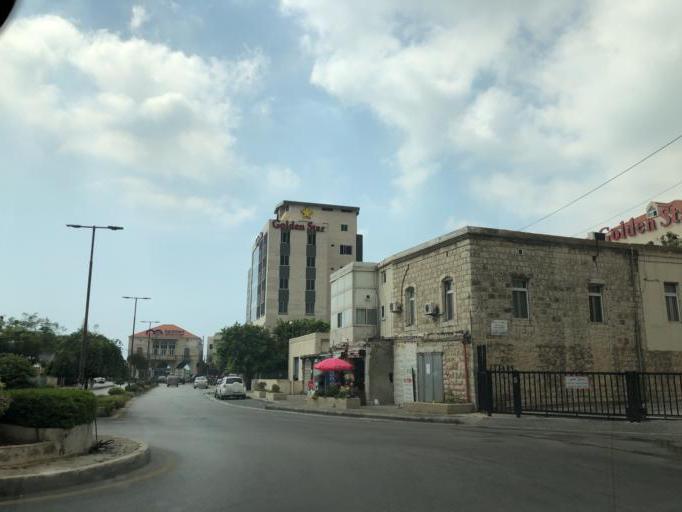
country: LB
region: Mont-Liban
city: Djounie
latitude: 33.9877
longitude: 35.6389
